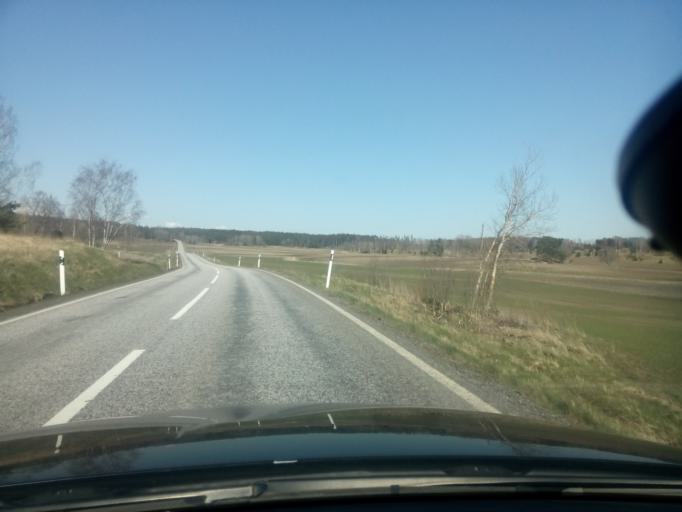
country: SE
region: Soedermanland
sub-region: Nykopings Kommun
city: Stigtomta
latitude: 58.9194
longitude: 16.8281
